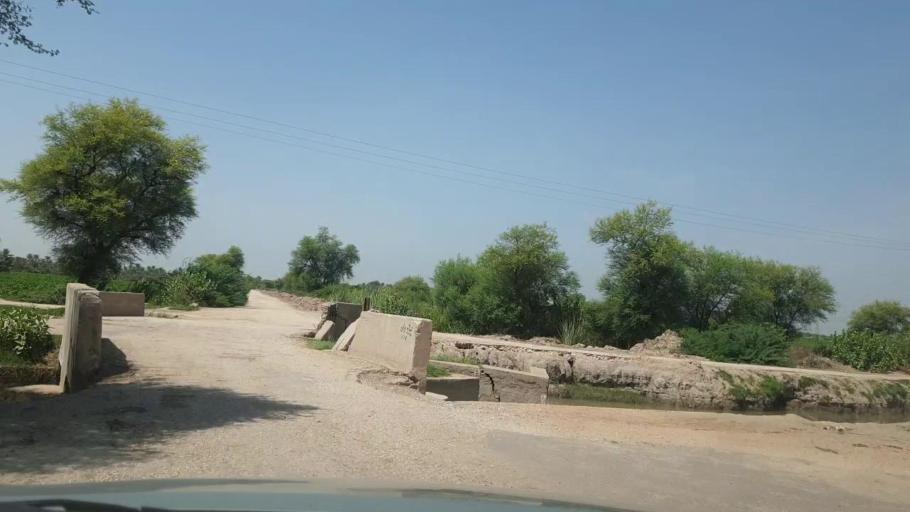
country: PK
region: Sindh
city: Rohri
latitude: 27.6660
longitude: 68.9804
